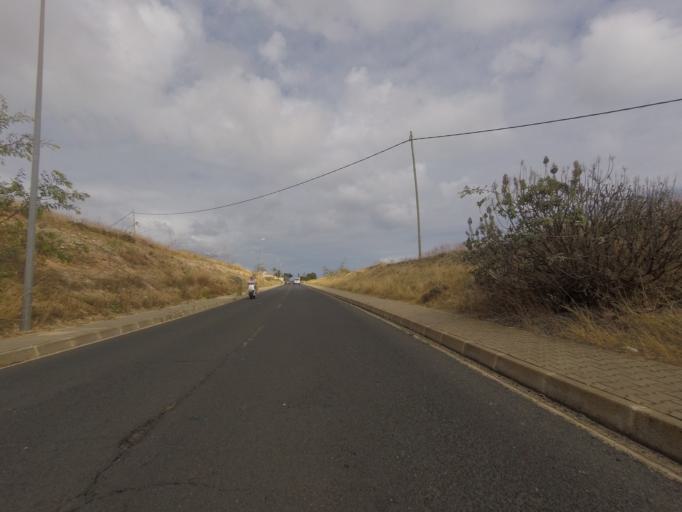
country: PT
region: Madeira
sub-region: Porto Santo
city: Vila de Porto Santo
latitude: 33.0554
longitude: -16.3497
